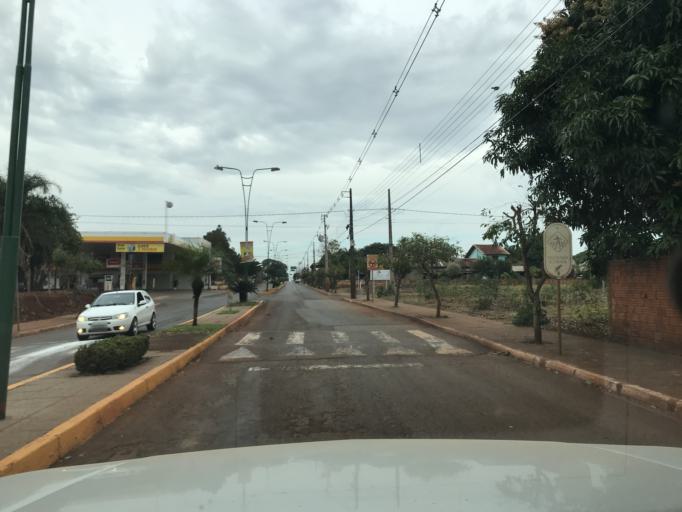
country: BR
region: Parana
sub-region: Marechal Candido Rondon
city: Marechal Candido Rondon
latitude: -24.4613
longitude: -53.9498
